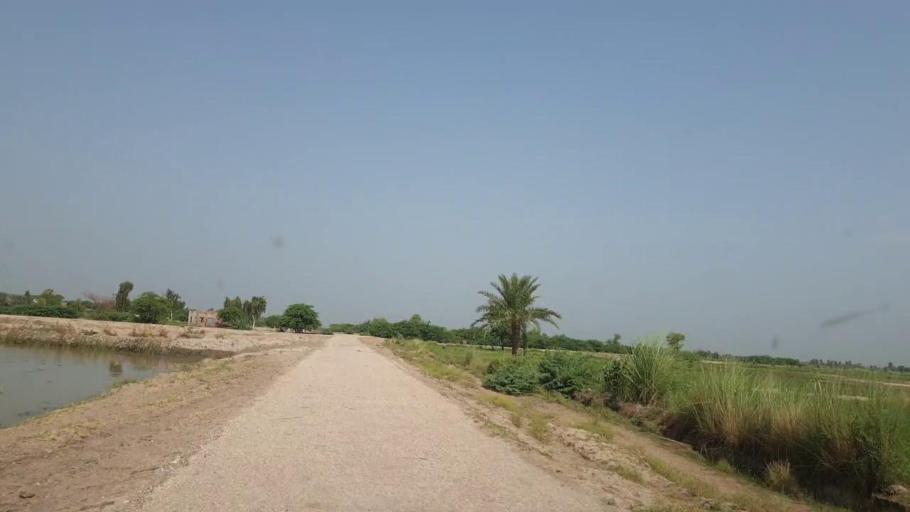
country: PK
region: Sindh
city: Lakhi
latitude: 27.8272
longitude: 68.6890
